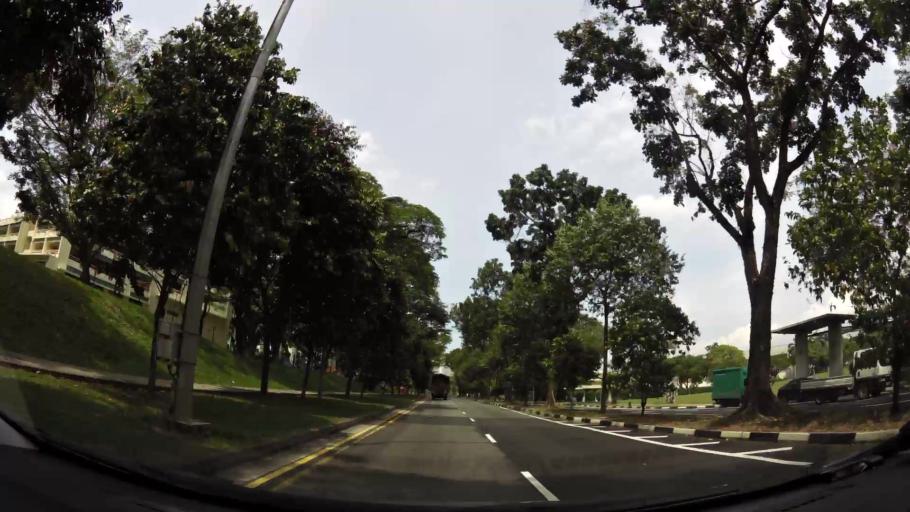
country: MY
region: Johor
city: Johor Bahru
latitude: 1.3490
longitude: 103.7141
